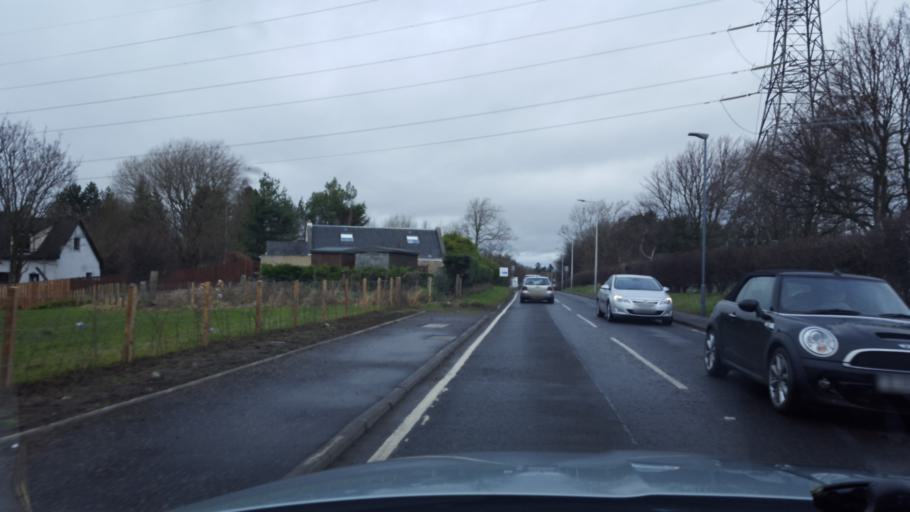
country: GB
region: Scotland
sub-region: Edinburgh
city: Currie
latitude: 55.9018
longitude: -3.3104
